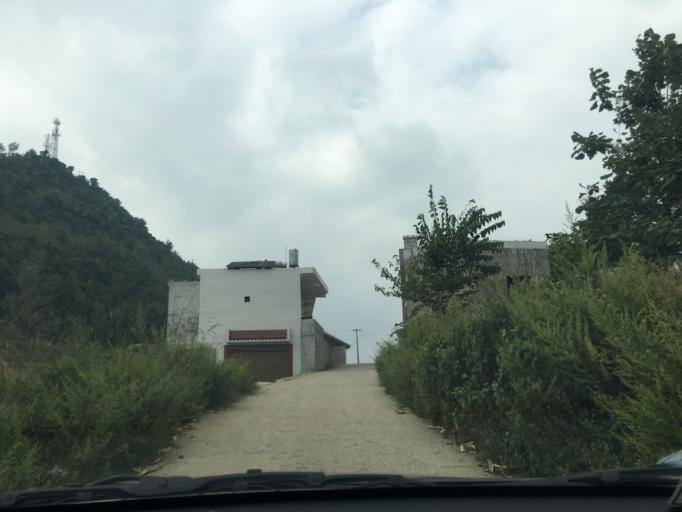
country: CN
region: Guizhou Sheng
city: Anshun
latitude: 25.5732
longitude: 105.6218
